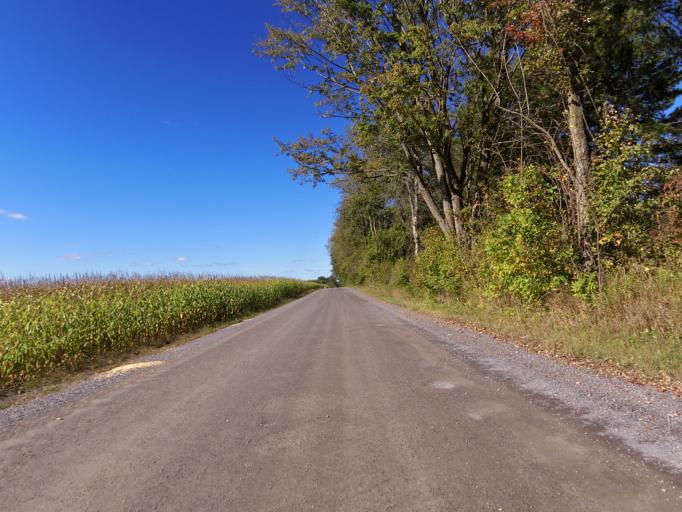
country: CA
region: Ontario
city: Clarence-Rockland
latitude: 45.4049
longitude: -75.3696
